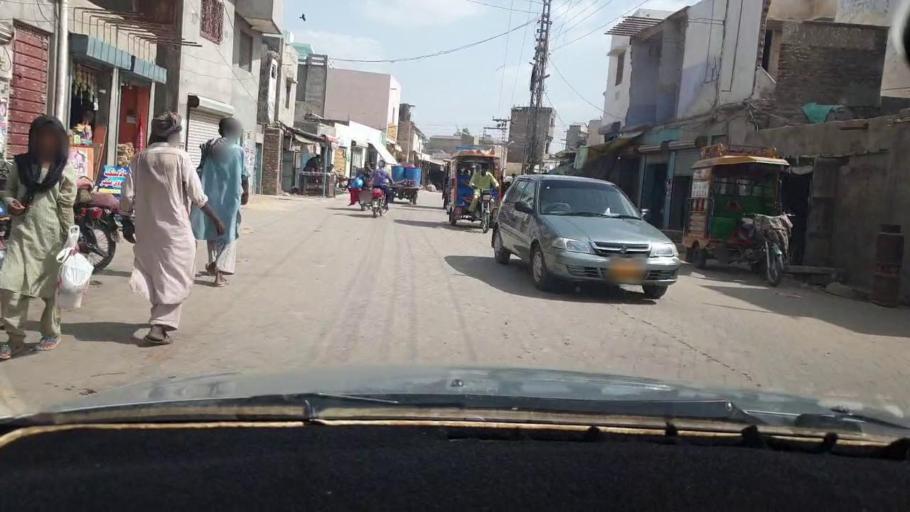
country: PK
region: Sindh
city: Digri
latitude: 25.0730
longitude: 69.2155
